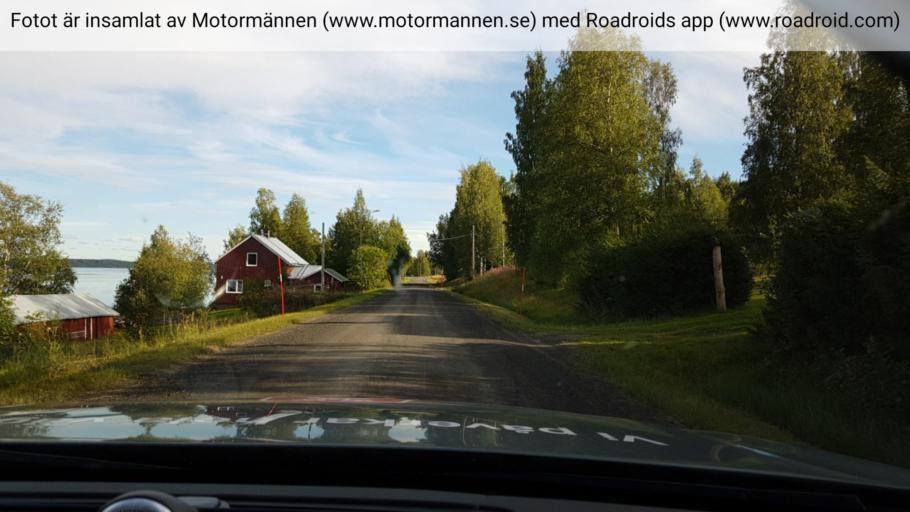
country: SE
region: Jaemtland
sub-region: Stroemsunds Kommun
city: Stroemsund
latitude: 64.1162
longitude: 15.8107
